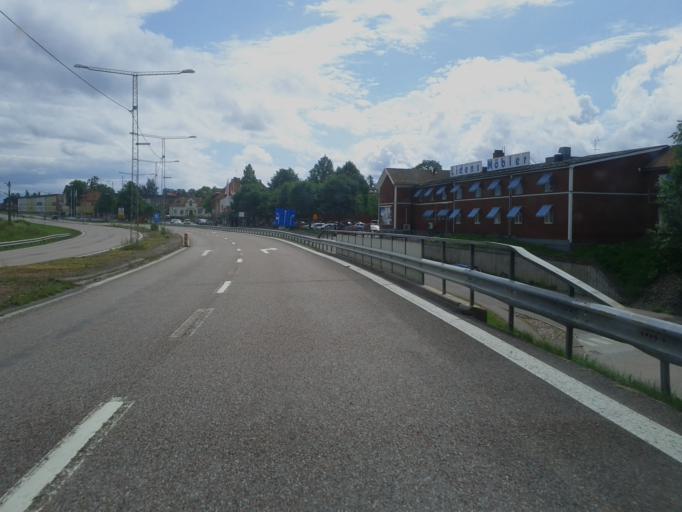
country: SE
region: Dalarna
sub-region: Saters Kommun
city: Saeter
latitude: 60.3488
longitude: 15.7488
